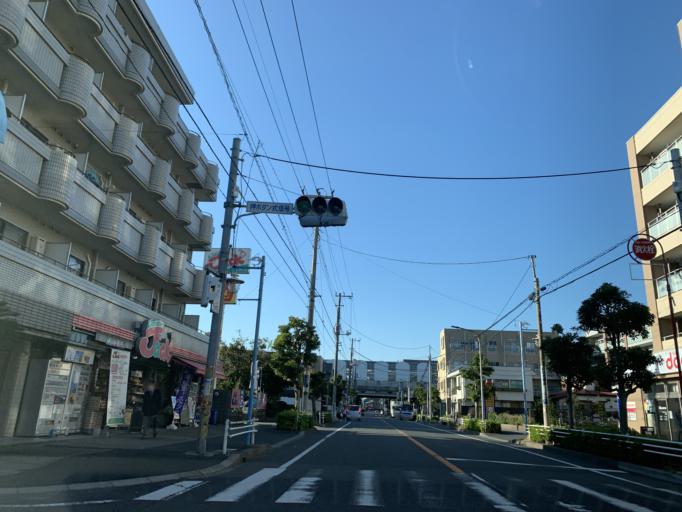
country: JP
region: Tokyo
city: Urayasu
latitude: 35.6900
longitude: 139.9255
